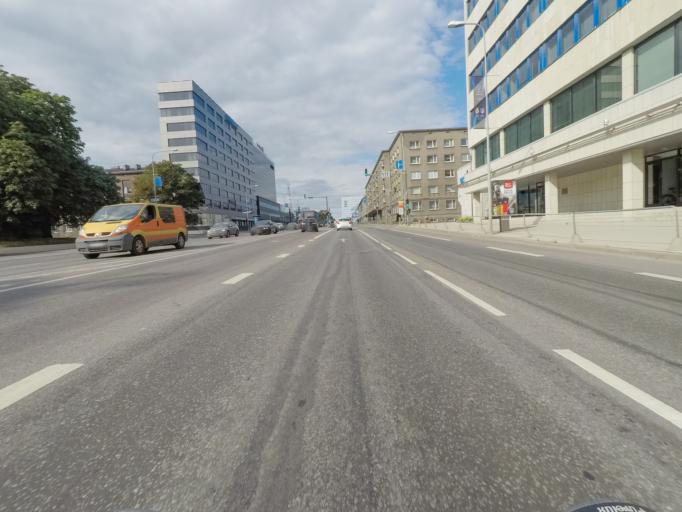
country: EE
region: Harju
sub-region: Tallinna linn
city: Tallinn
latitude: 59.4282
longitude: 24.7492
